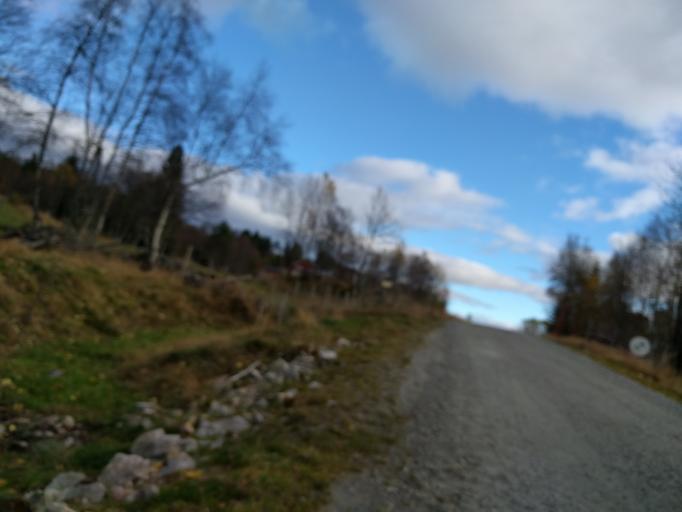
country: NO
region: Aust-Agder
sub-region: Evje og Hornnes
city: Evje
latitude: 58.6528
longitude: 7.9479
